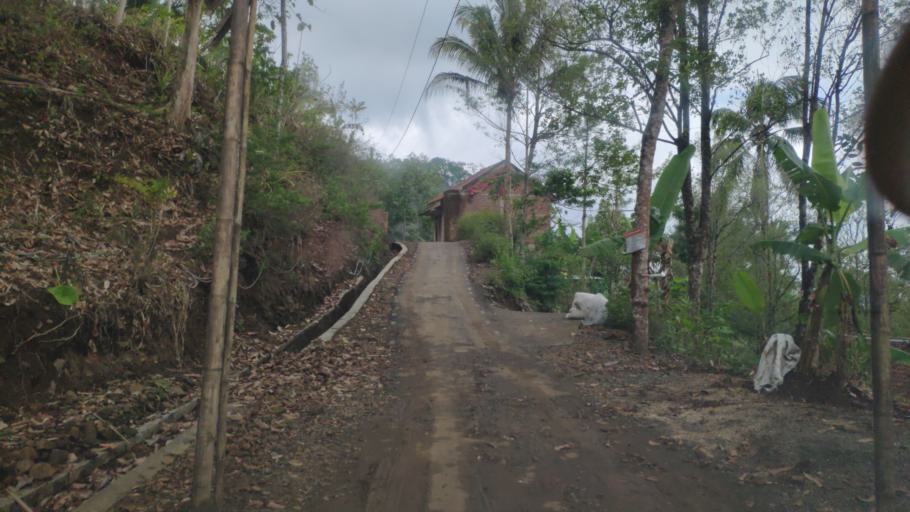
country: ID
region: Central Java
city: Gombong
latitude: -7.5308
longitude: 109.4273
